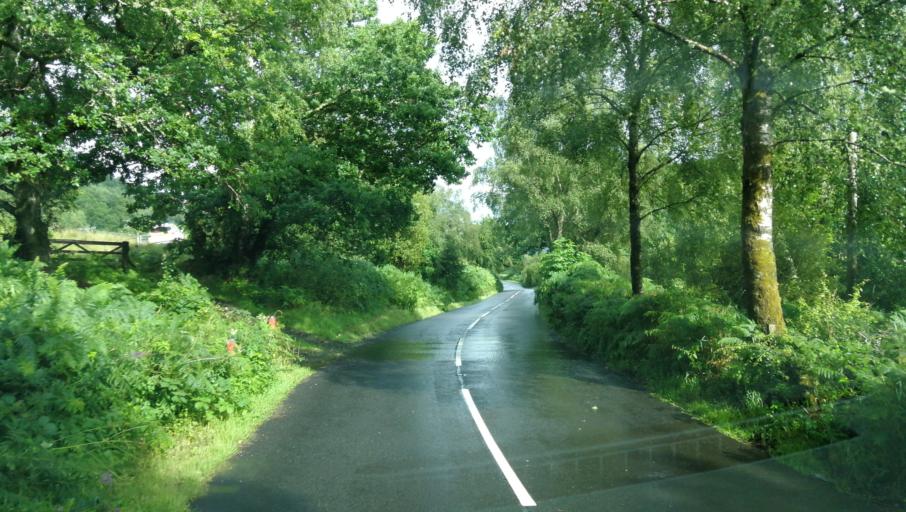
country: GB
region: Scotland
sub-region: Stirling
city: Callander
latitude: 56.2272
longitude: -4.3369
